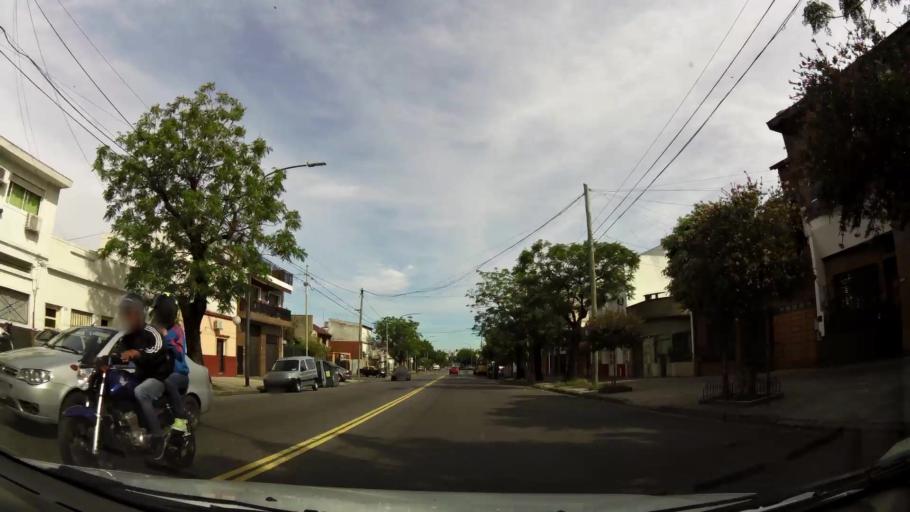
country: AR
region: Buenos Aires F.D.
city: Villa Lugano
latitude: -34.6498
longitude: -58.4833
